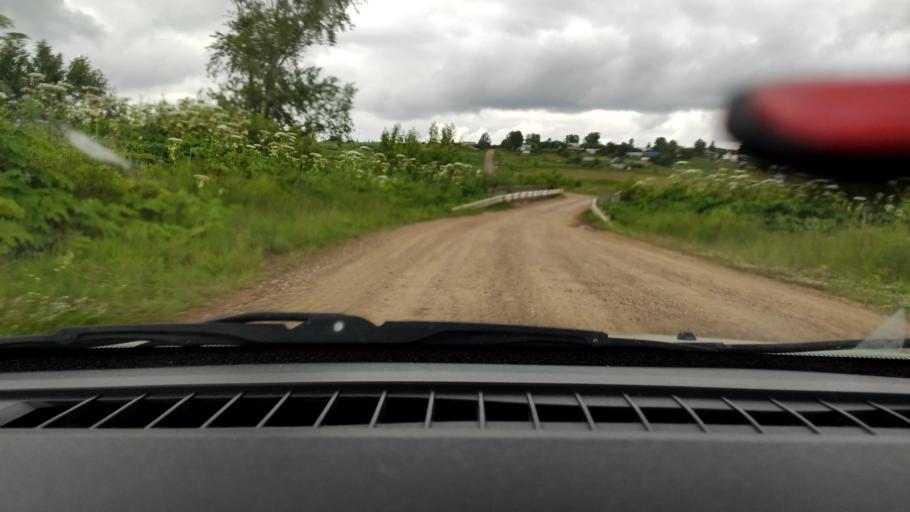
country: RU
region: Perm
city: Chaykovskaya
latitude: 58.1376
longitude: 55.5622
